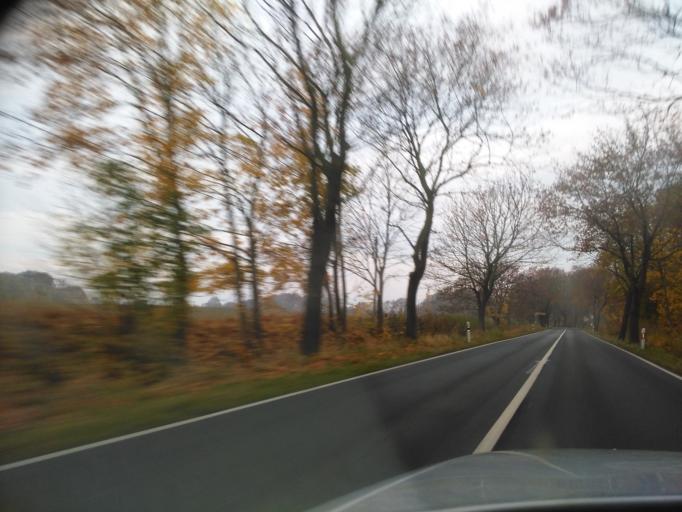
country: DE
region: Mecklenburg-Vorpommern
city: Altefahr
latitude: 54.3231
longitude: 13.1504
